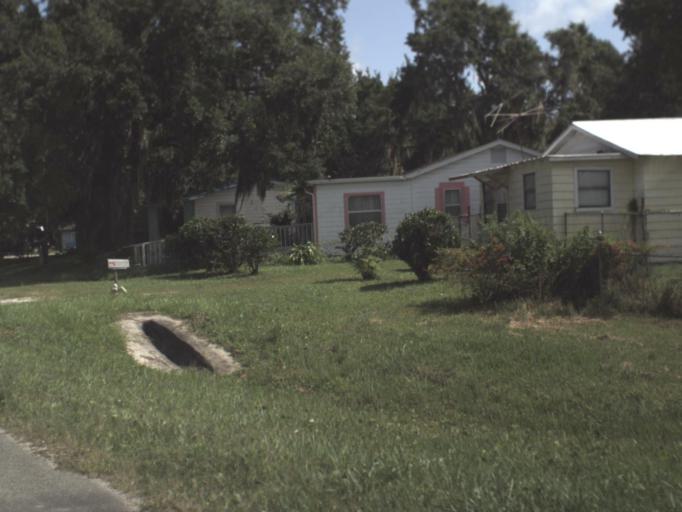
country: US
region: Florida
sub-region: Hernando County
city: Brooksville
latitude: 28.5474
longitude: -82.3808
